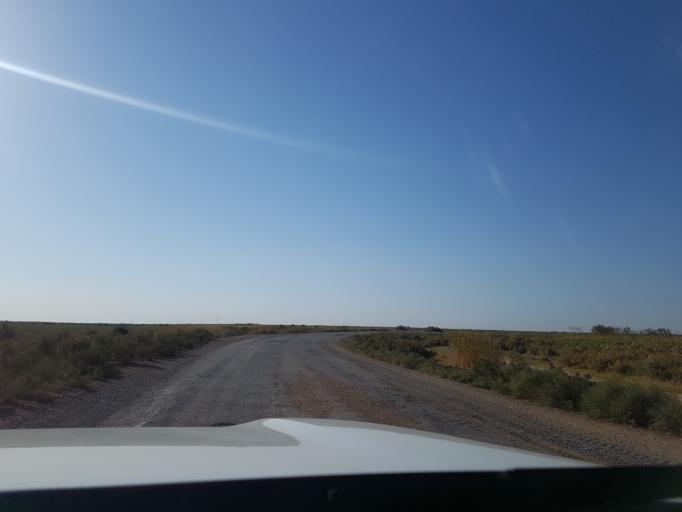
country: IR
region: Razavi Khorasan
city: Sarakhs
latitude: 36.9973
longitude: 61.3820
